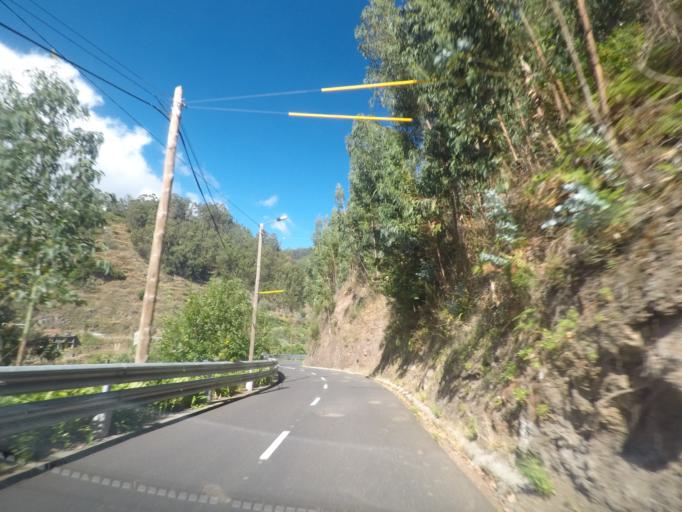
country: PT
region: Madeira
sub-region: Ribeira Brava
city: Campanario
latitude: 32.6871
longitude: -17.0309
